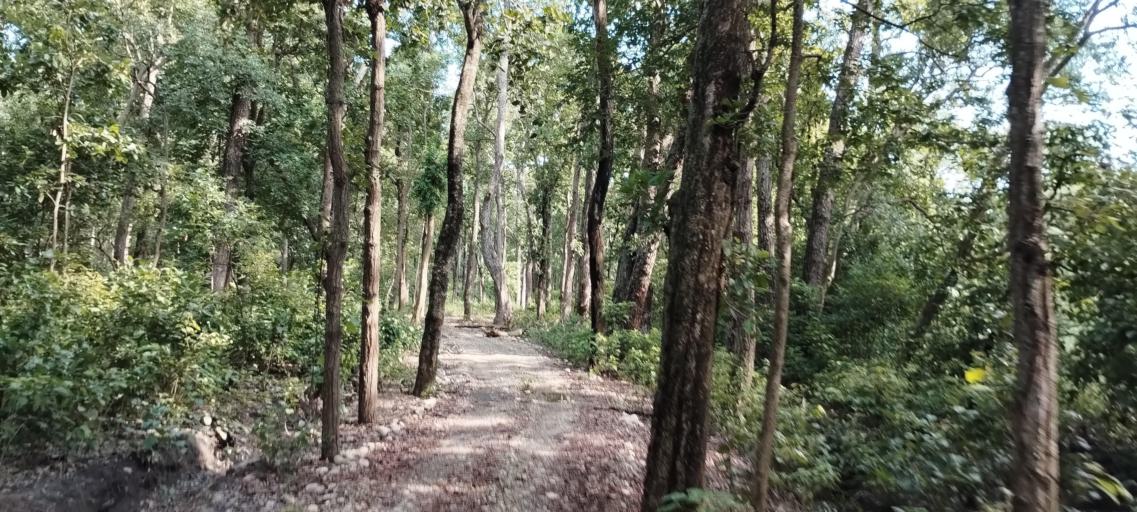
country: NP
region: Far Western
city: Tikapur
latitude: 28.5593
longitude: 81.2660
